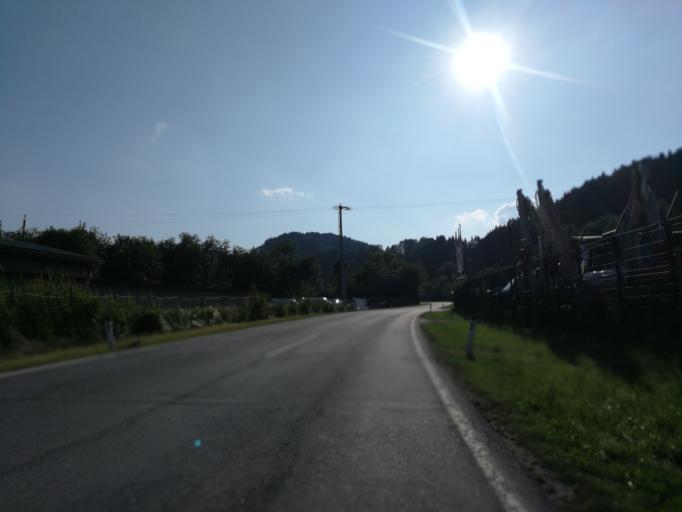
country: AT
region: Salzburg
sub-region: Politischer Bezirk Salzburg-Umgebung
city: Plainfeld
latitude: 47.8520
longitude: 13.2030
